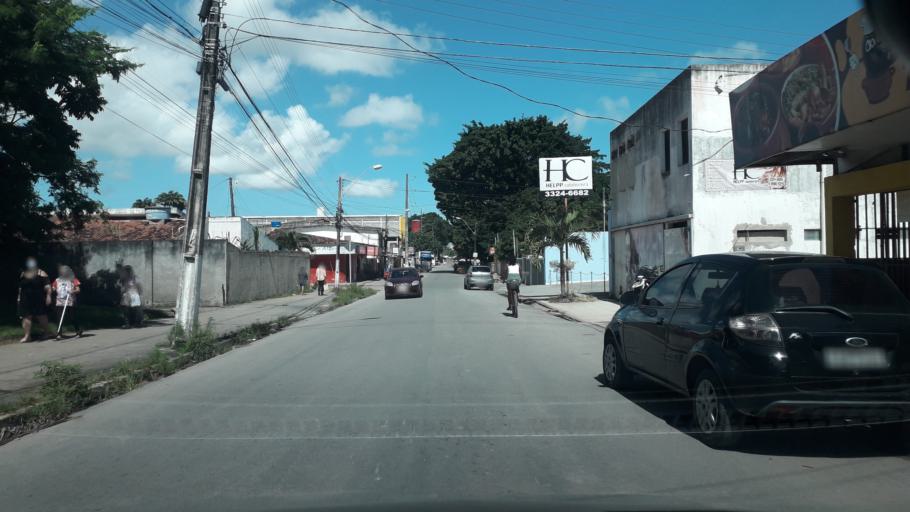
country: BR
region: Alagoas
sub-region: Satuba
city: Satuba
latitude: -9.5808
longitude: -35.7699
